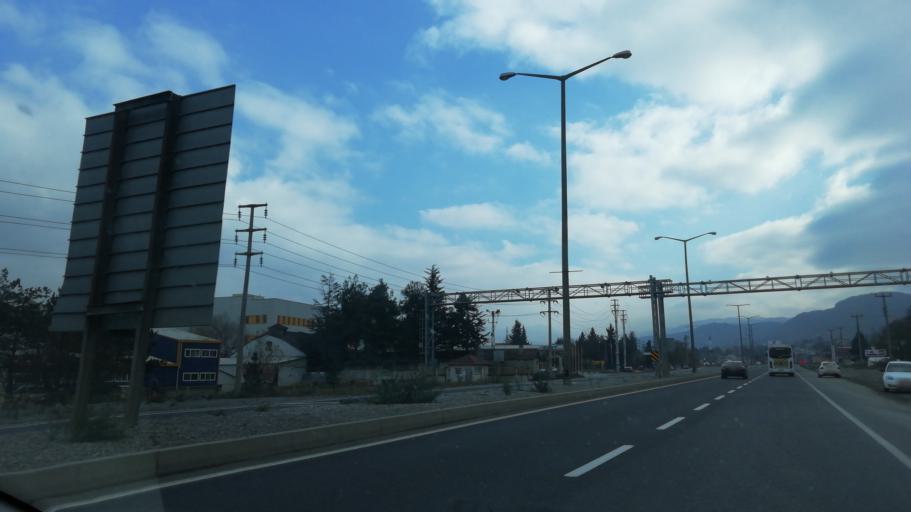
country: TR
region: Duzce
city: Kaynasli
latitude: 40.7807
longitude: 31.2808
